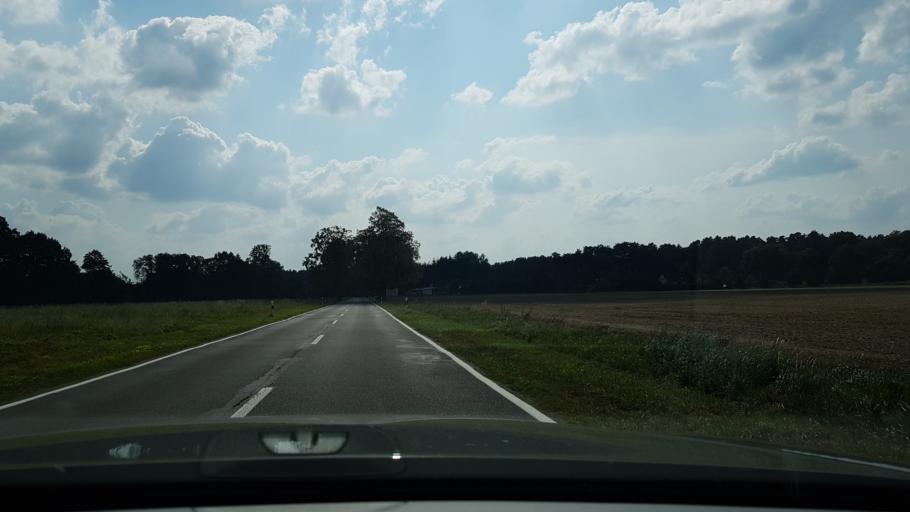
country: DE
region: Brandenburg
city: Lindow
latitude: 52.9958
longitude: 12.9729
